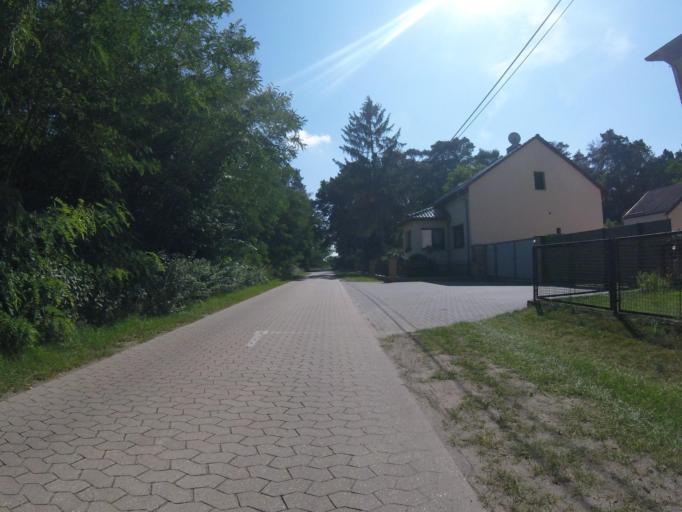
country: DE
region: Brandenburg
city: Bestensee
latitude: 52.2488
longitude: 13.6989
